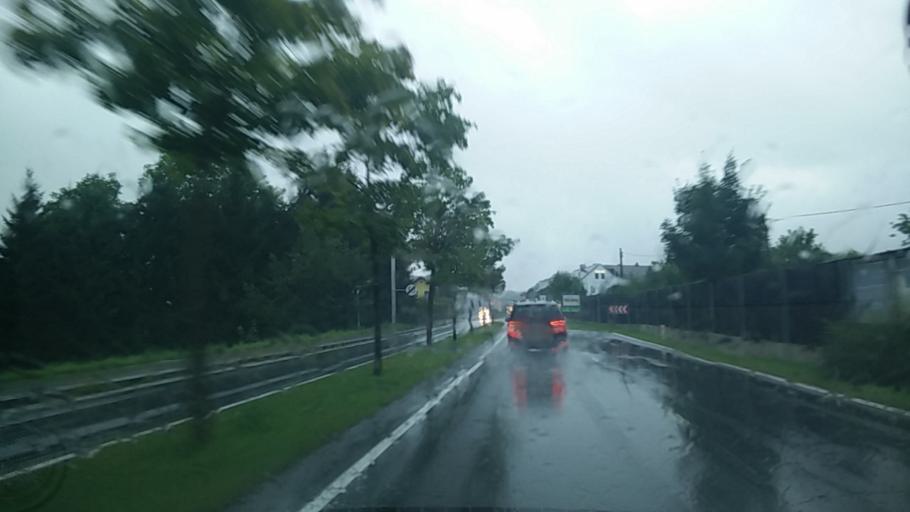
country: AT
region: Carinthia
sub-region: Politischer Bezirk Villach Land
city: Wernberg
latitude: 46.6220
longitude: 13.9421
